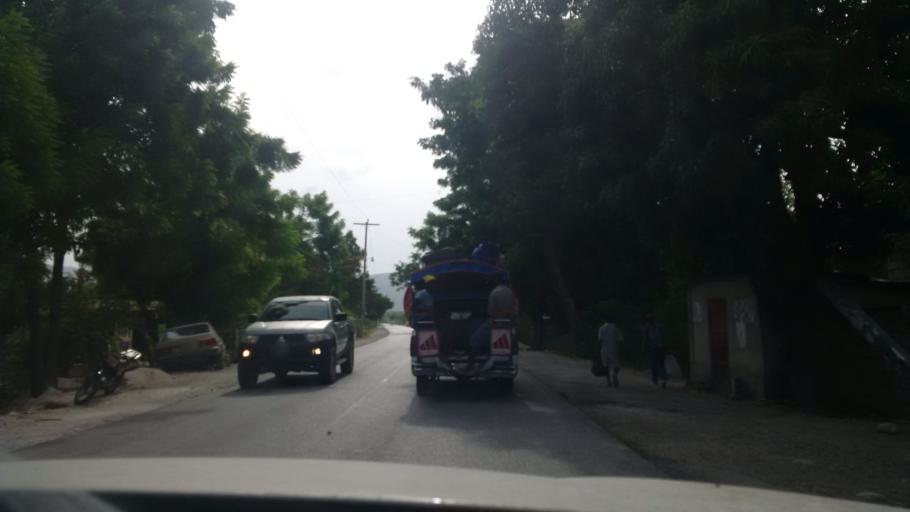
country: HT
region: Ouest
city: Grangwav
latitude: 18.4247
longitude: -72.7433
